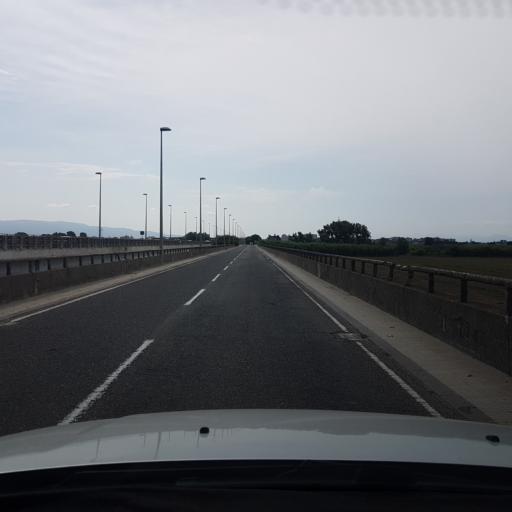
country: IT
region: Sardinia
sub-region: Provincia di Oristano
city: Donigala Fenugheddu
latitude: 39.9213
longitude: 8.5818
